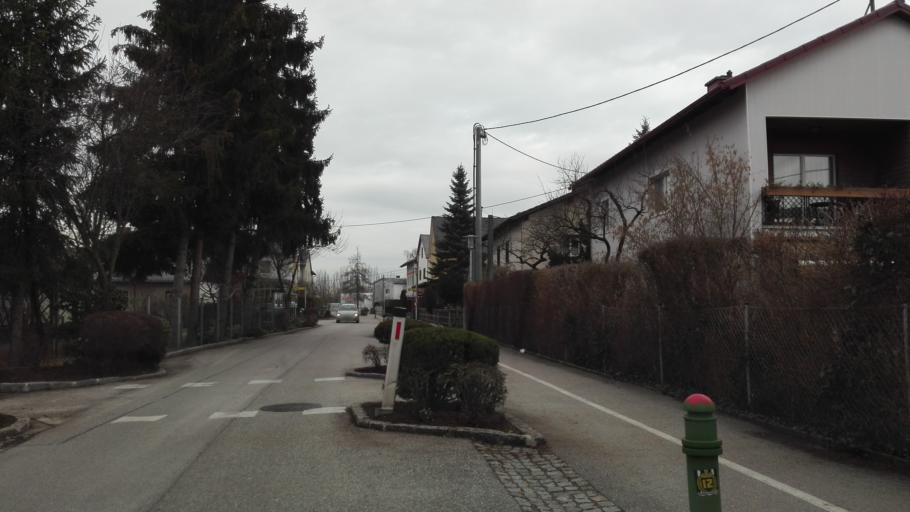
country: AT
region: Upper Austria
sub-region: Politischer Bezirk Linz-Land
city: Traun
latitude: 48.2373
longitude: 14.2311
